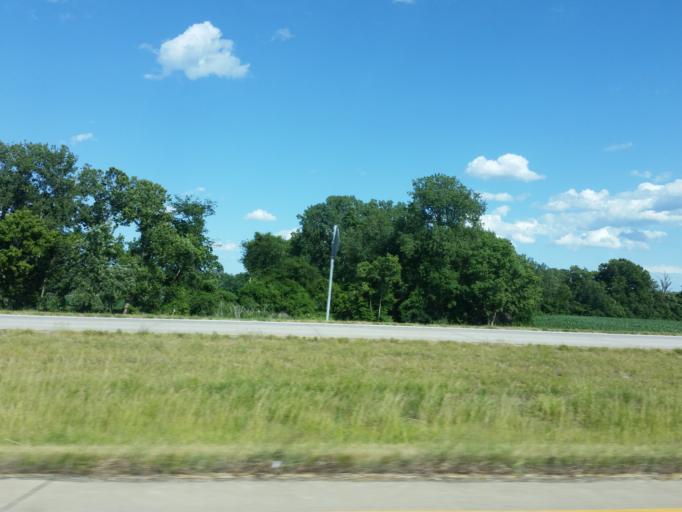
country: US
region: Missouri
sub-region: Lewis County
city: Canton
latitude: 40.1767
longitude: -91.5253
